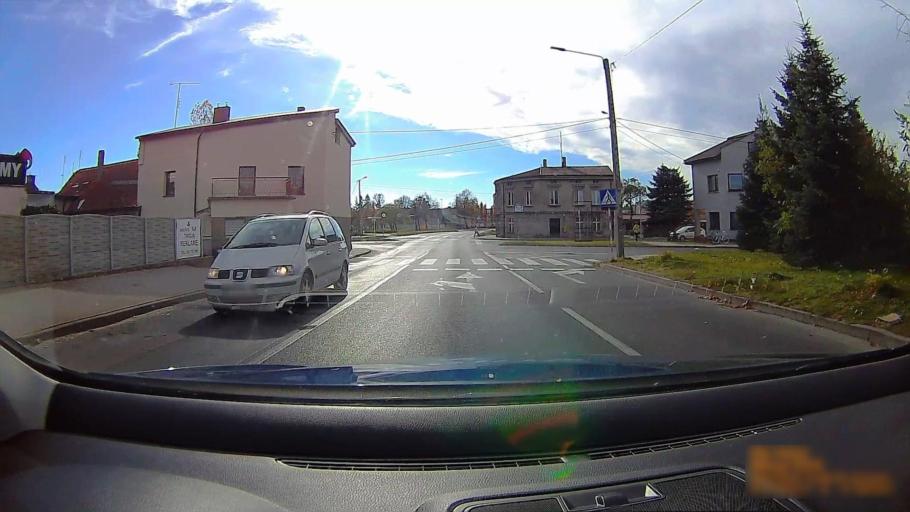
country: PL
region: Greater Poland Voivodeship
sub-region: Powiat ostrzeszowski
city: Ostrzeszow
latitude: 51.4259
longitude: 17.9386
